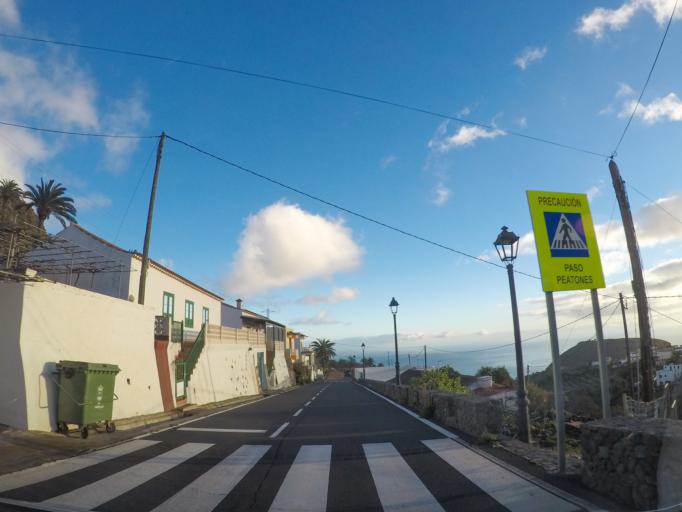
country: ES
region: Canary Islands
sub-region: Provincia de Santa Cruz de Tenerife
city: Alajero
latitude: 28.0646
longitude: -17.2374
